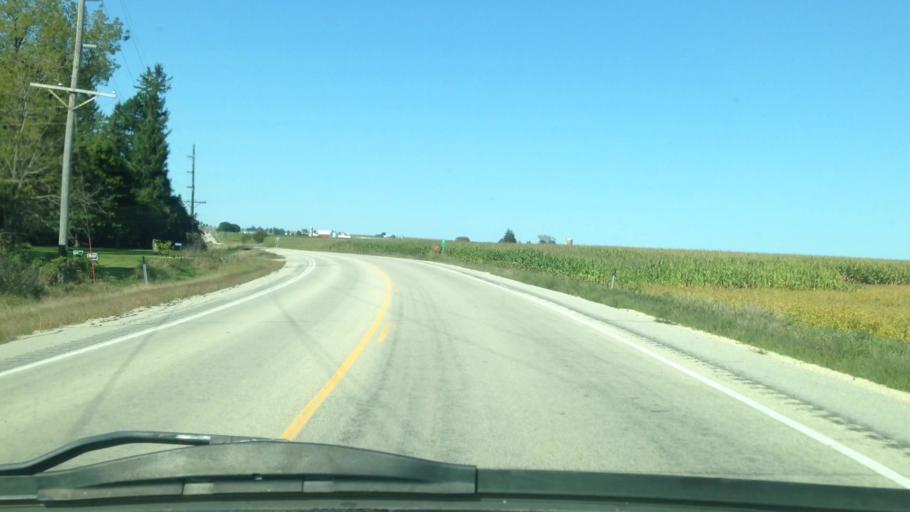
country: US
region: Minnesota
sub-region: Fillmore County
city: Rushford
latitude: 43.8626
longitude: -91.7406
